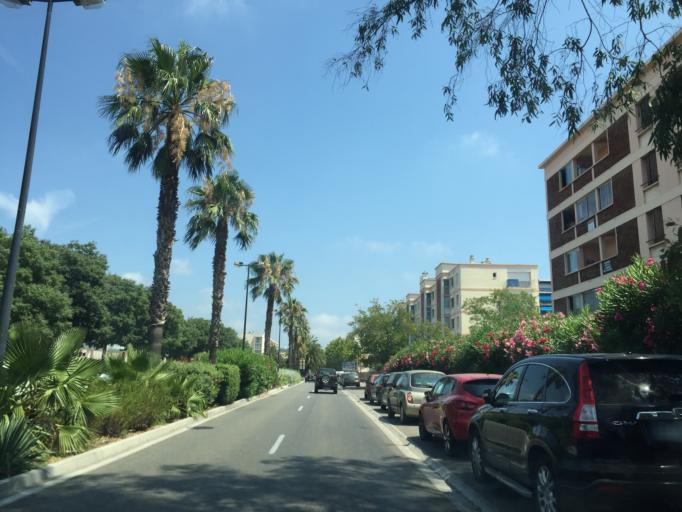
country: FR
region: Provence-Alpes-Cote d'Azur
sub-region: Departement du Var
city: Frejus
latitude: 43.4267
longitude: 6.7539
